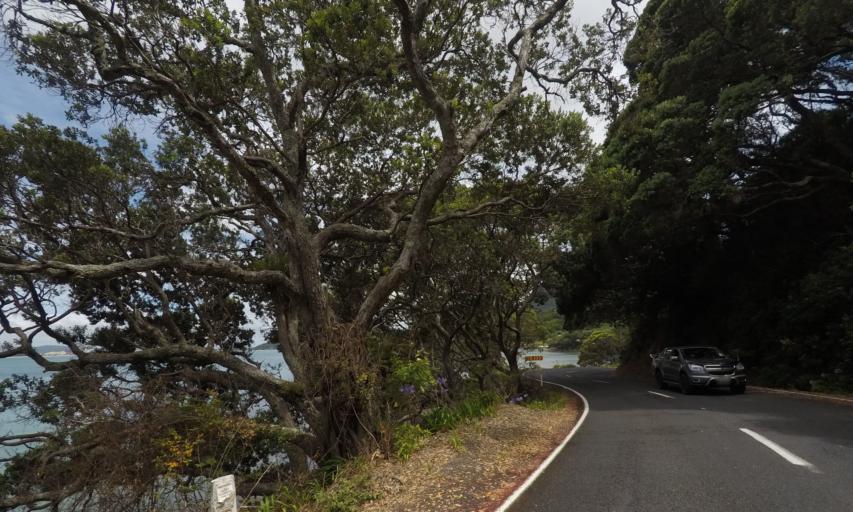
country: NZ
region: Northland
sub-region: Whangarei
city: Ruakaka
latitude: -35.8361
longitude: 174.5332
